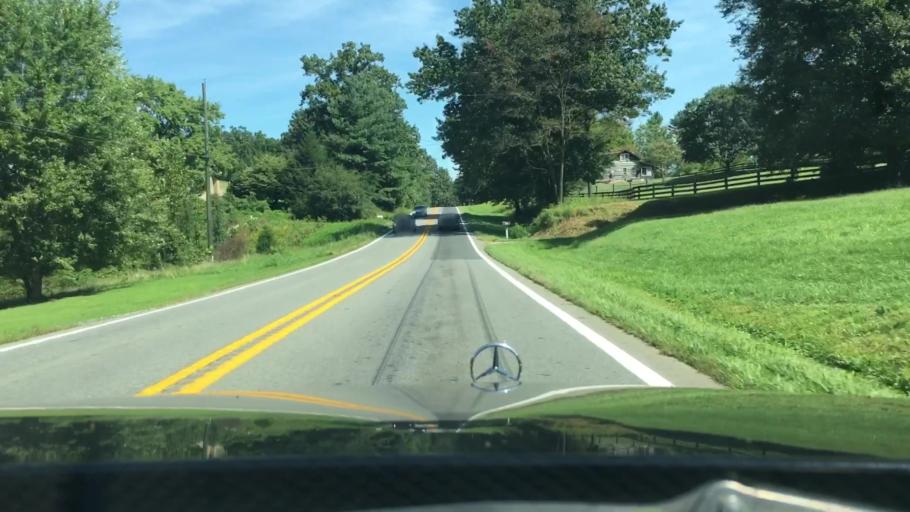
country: US
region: Virginia
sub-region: Nelson County
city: Nellysford
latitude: 37.9251
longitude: -78.8385
